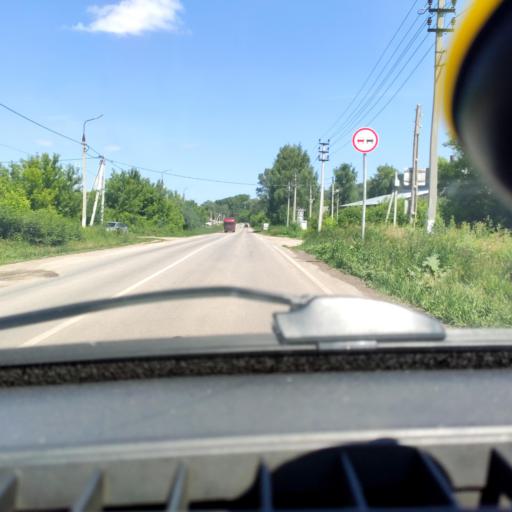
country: RU
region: Samara
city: Zhigulevsk
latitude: 53.3874
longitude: 49.5069
